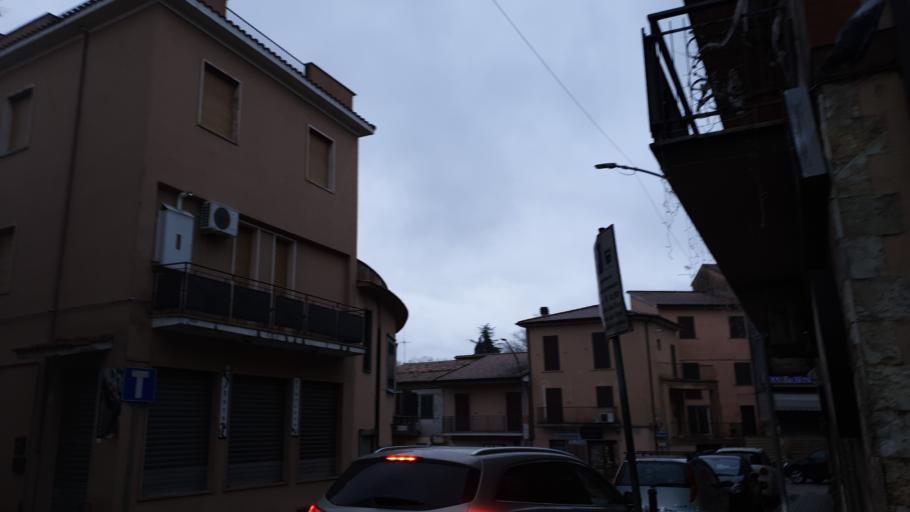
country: IT
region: Latium
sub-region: Provincia di Frosinone
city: Ceccano
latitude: 41.5674
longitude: 13.3305
